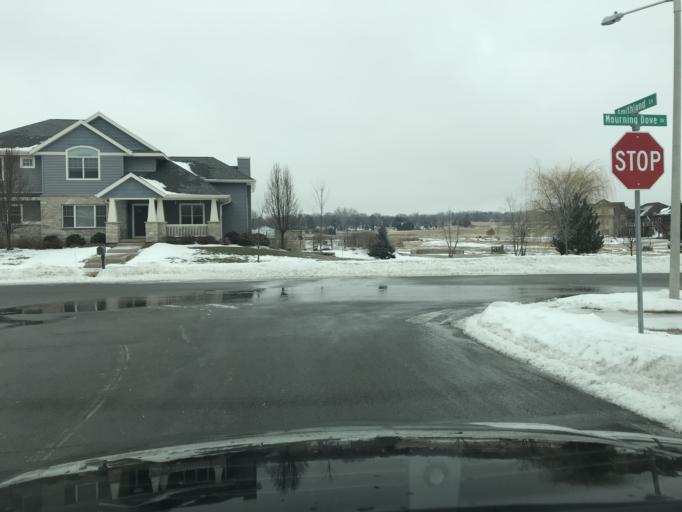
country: US
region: Wisconsin
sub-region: Dane County
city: Cottage Grove
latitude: 43.0957
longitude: -89.2144
